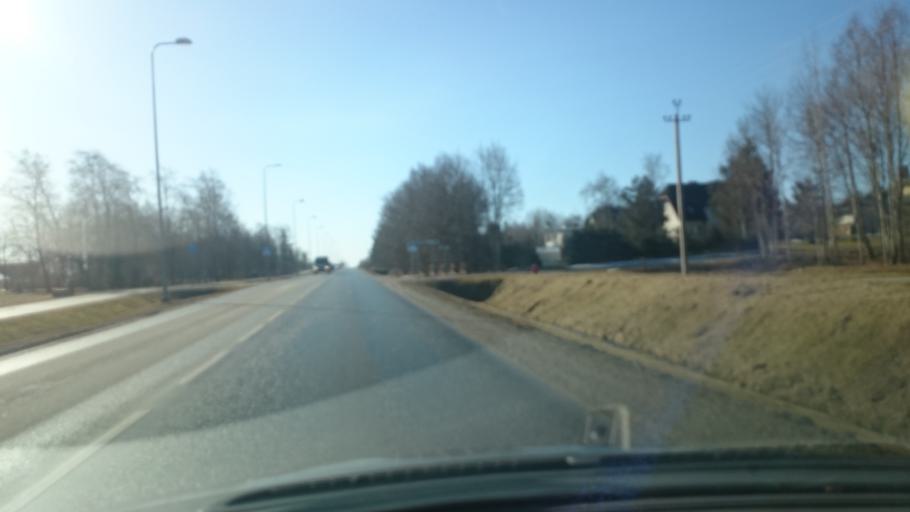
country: EE
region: Harju
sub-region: Saku vald
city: Saku
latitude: 59.2991
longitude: 24.6518
